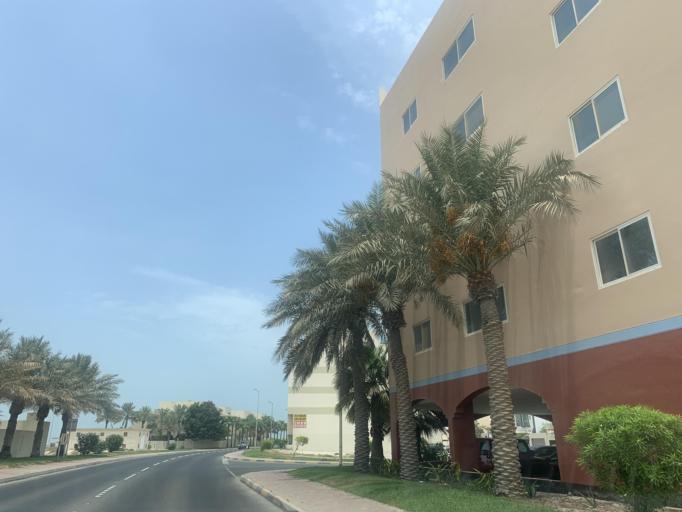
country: BH
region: Muharraq
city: Al Hadd
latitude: 26.2972
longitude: 50.6580
